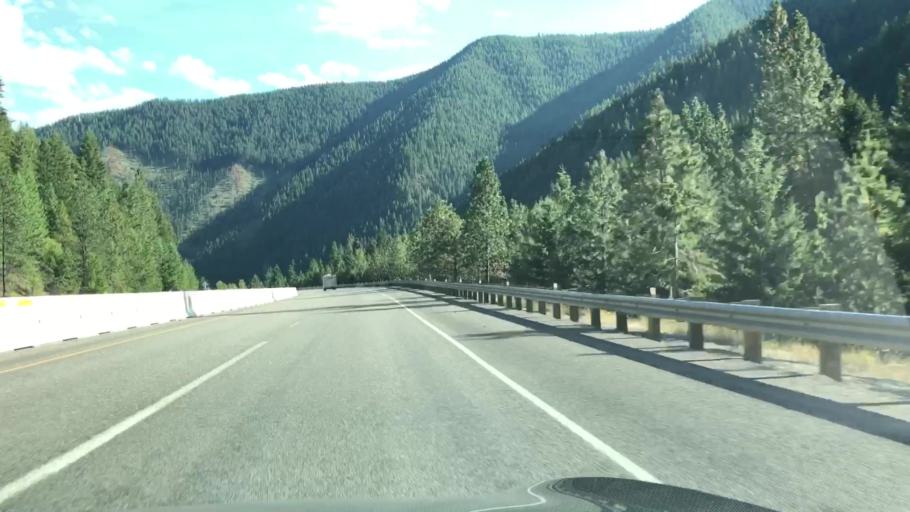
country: US
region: Montana
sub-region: Sanders County
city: Thompson Falls
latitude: 47.3105
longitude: -115.2090
